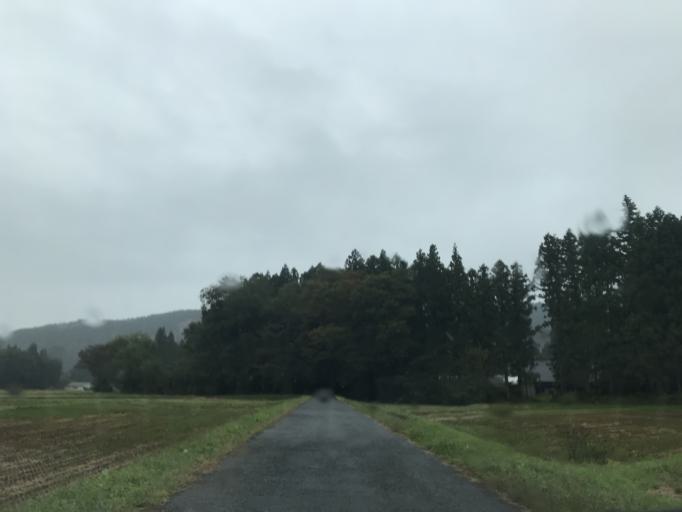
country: JP
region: Iwate
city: Ichinoseki
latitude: 38.9753
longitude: 140.9591
